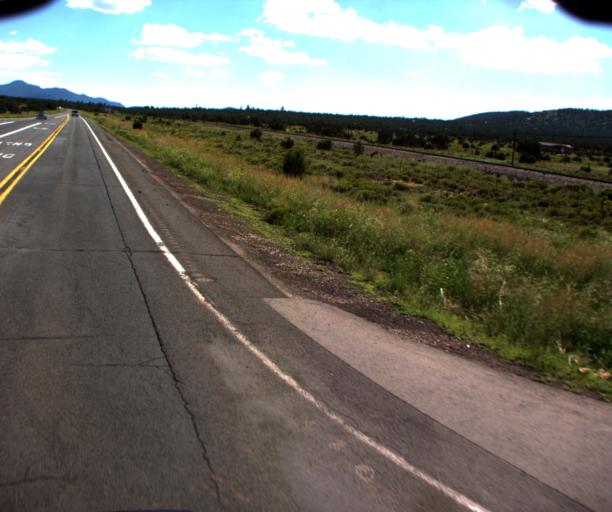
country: US
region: Arizona
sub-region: Coconino County
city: Williams
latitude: 35.3675
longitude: -112.1650
